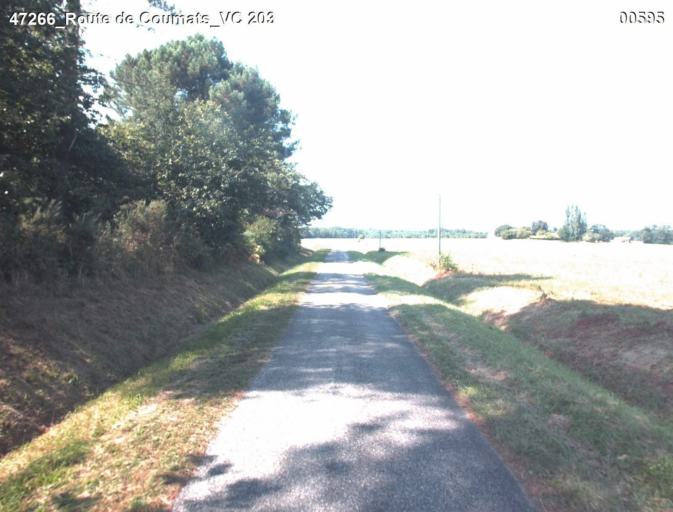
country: FR
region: Aquitaine
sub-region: Departement des Landes
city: Gabarret
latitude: 44.0126
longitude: 0.0911
